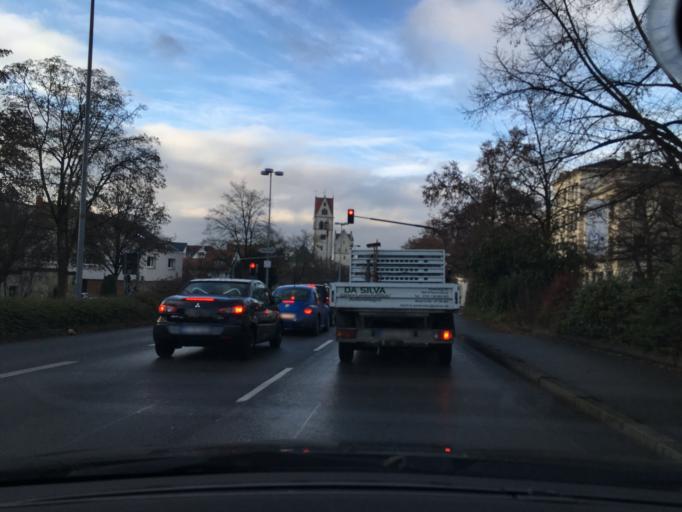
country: DE
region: Baden-Wuerttemberg
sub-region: Tuebingen Region
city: Ravensburg
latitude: 47.7818
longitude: 9.6179
